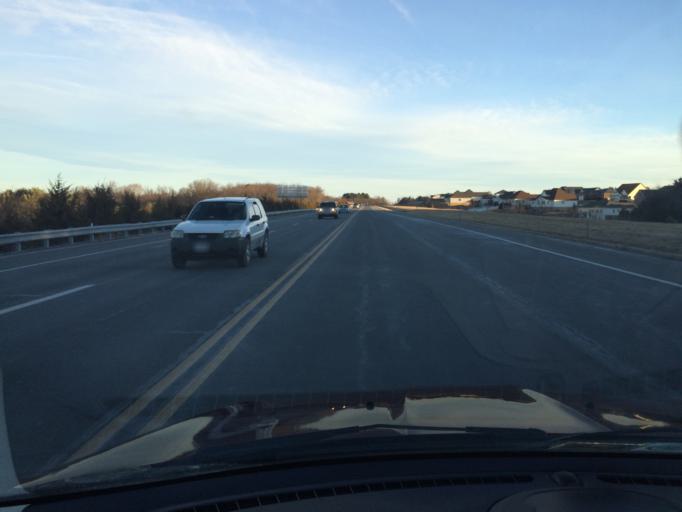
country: US
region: Virginia
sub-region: City of Staunton
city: Staunton
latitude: 38.1648
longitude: -79.1092
